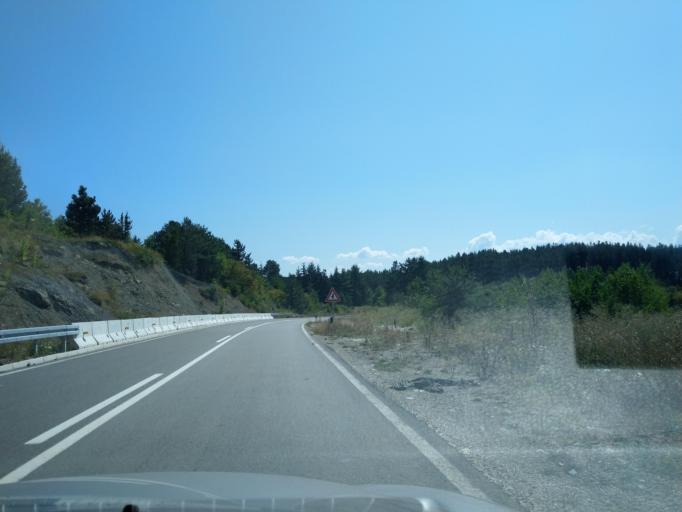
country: RS
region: Central Serbia
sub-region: Zlatiborski Okrug
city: Sjenica
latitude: 43.3090
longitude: 19.9118
